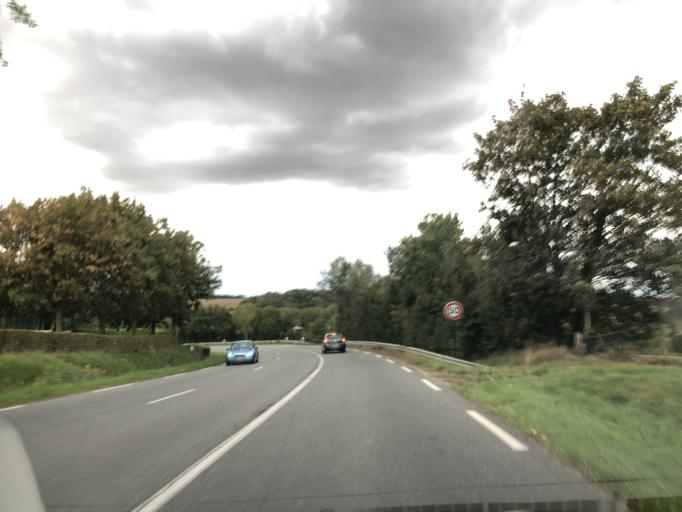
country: FR
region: Picardie
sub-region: Departement de la Somme
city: Chepy
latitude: 50.1004
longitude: 1.7263
